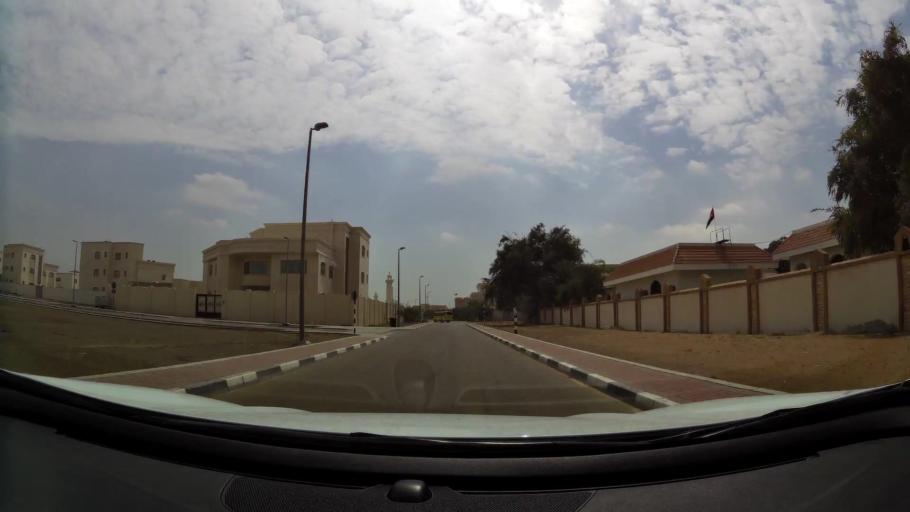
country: AE
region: Abu Dhabi
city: Al Ain
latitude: 24.2015
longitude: 55.8063
